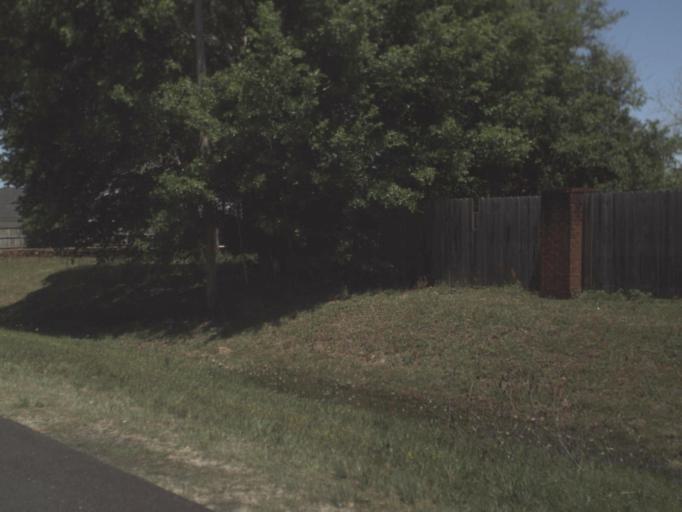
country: US
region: Florida
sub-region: Escambia County
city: Bellview
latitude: 30.4805
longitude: -87.3235
